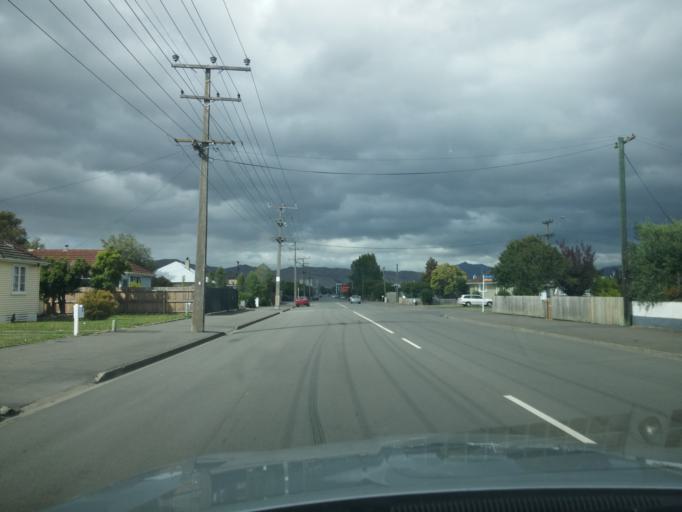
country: NZ
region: Marlborough
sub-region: Marlborough District
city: Blenheim
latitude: -41.5026
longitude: 173.9554
